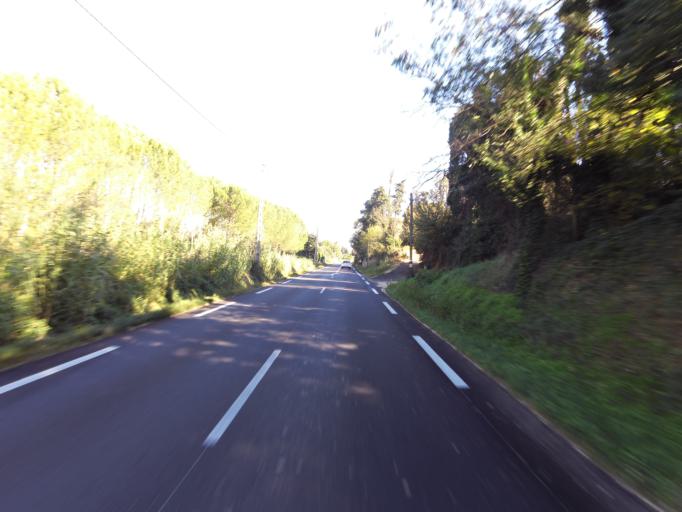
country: FR
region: Provence-Alpes-Cote d'Azur
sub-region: Departement du Vaucluse
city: Loriol-du-Comtat
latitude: 44.0686
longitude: 5.0207
